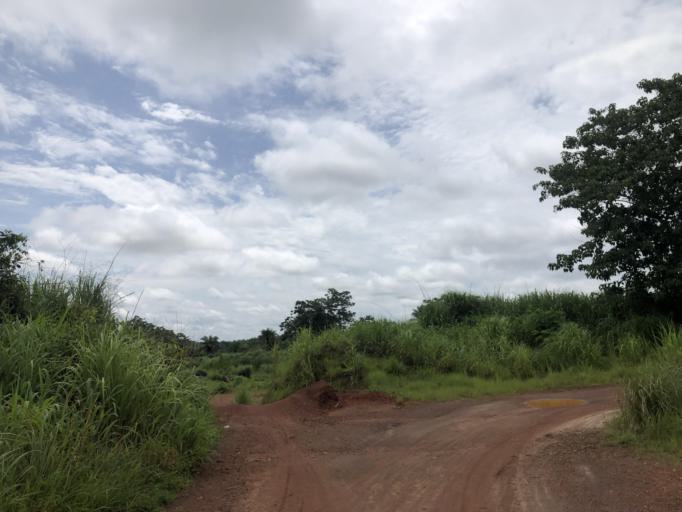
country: SL
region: Northern Province
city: Lunsar
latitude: 8.6710
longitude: -12.5301
